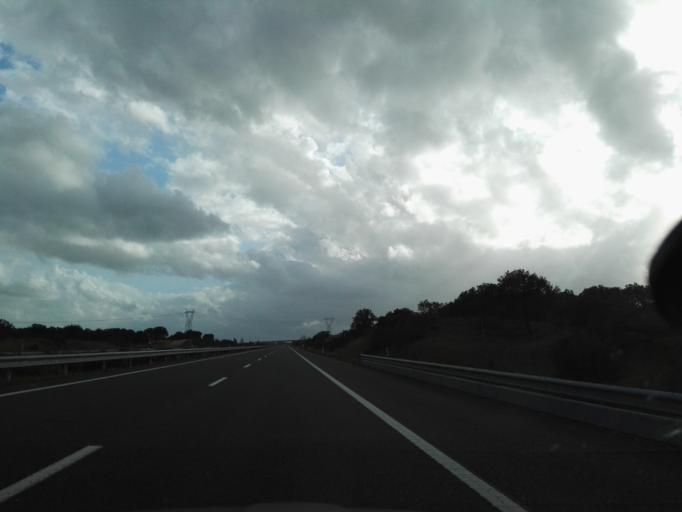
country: PT
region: Evora
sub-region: Evora
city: Evora
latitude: 38.7224
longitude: -7.7787
